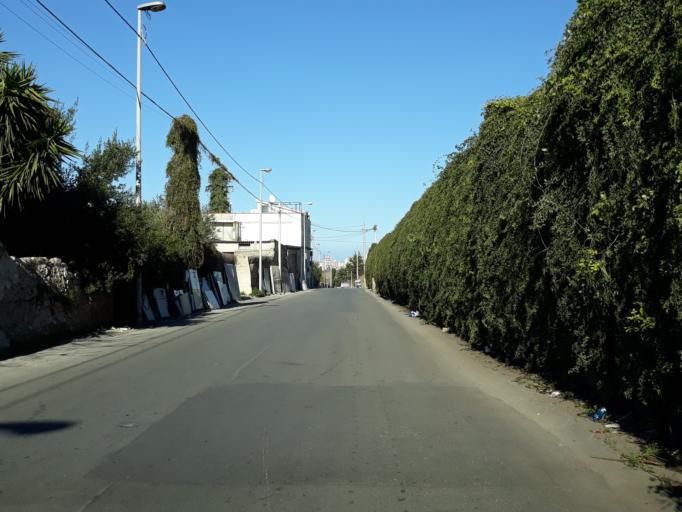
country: IT
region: Sicily
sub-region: Palermo
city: Ciaculli
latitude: 38.0864
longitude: 13.3807
